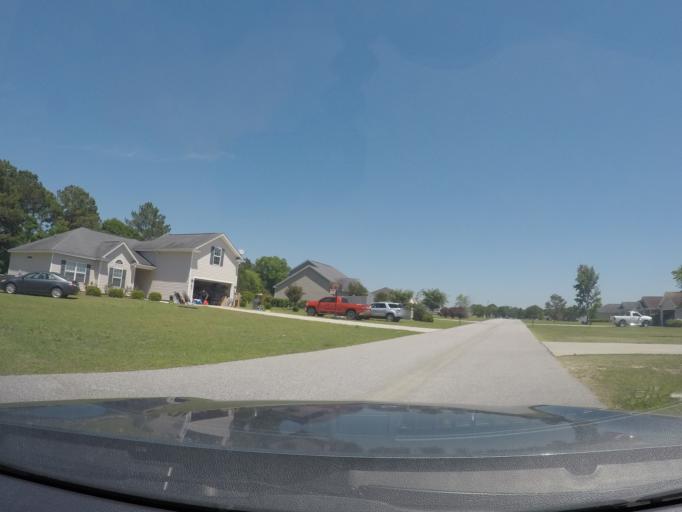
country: US
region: Georgia
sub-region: Bulloch County
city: Statesboro
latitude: 32.3544
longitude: -81.7592
